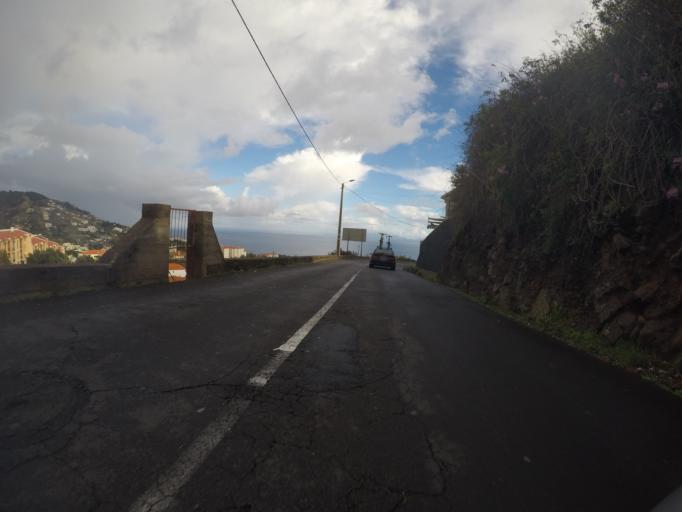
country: PT
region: Madeira
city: Canico
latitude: 32.6503
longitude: -16.8508
